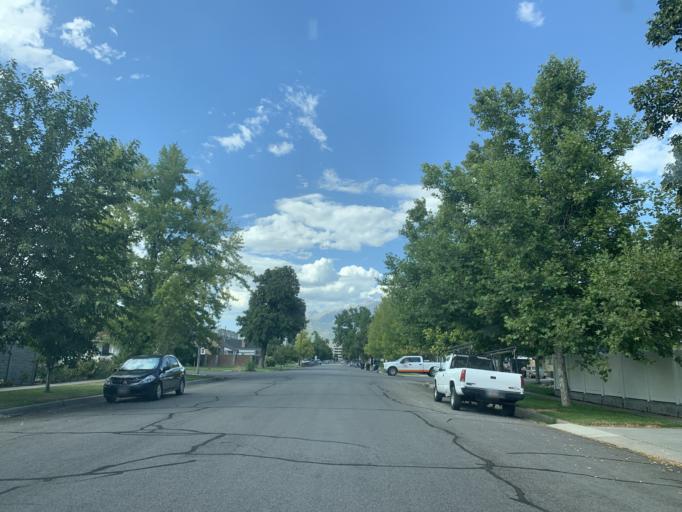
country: US
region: Utah
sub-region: Utah County
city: Provo
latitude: 40.2279
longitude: -111.6569
